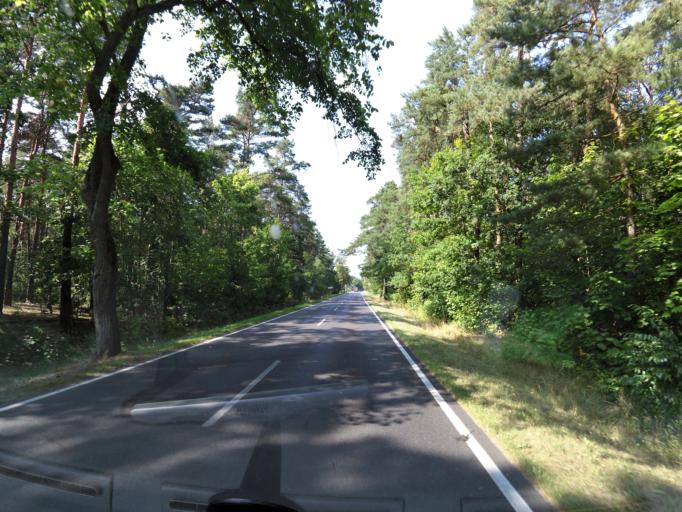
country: DE
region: Brandenburg
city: Zehdenick
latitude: 52.9650
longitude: 13.3652
